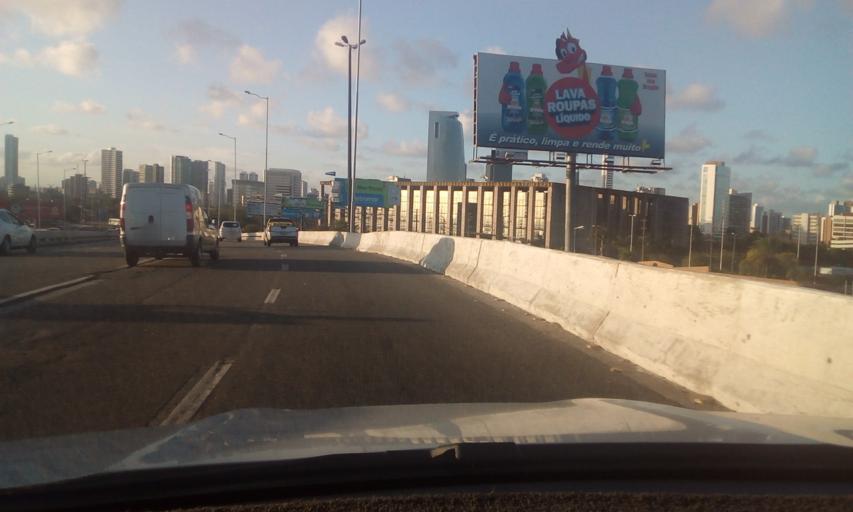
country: BR
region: Pernambuco
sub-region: Recife
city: Recife
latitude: -8.0729
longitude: -34.8939
